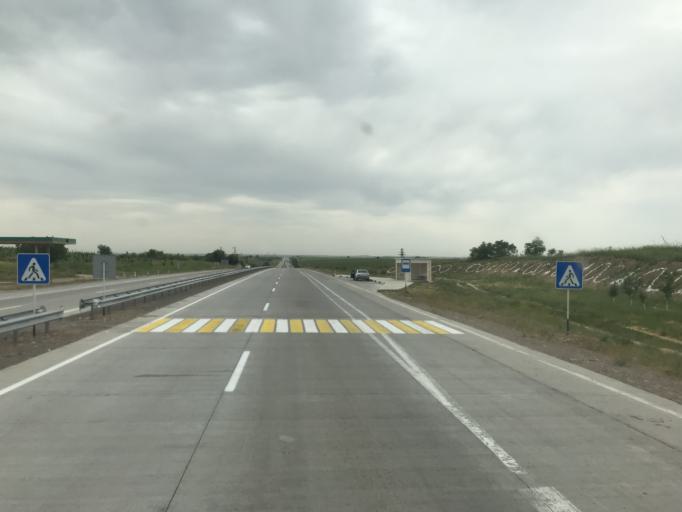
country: KZ
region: Ongtustik Qazaqstan
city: Qazyqurt
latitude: 41.6054
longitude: 69.4043
